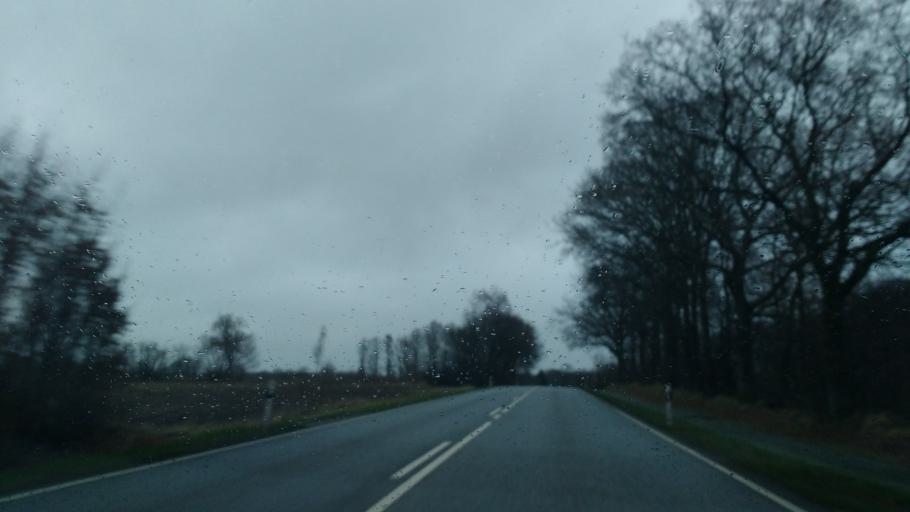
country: DE
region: Schleswig-Holstein
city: Jahrsdorf
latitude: 54.0509
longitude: 9.6262
